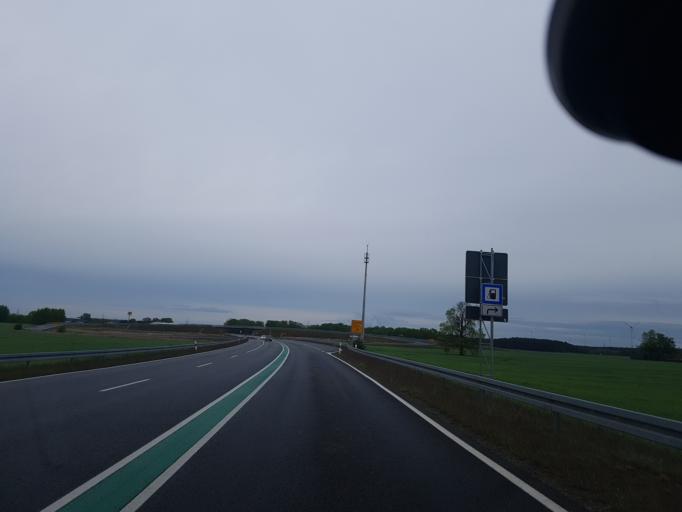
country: DE
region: Brandenburg
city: Drebkau
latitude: 51.6413
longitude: 14.2348
